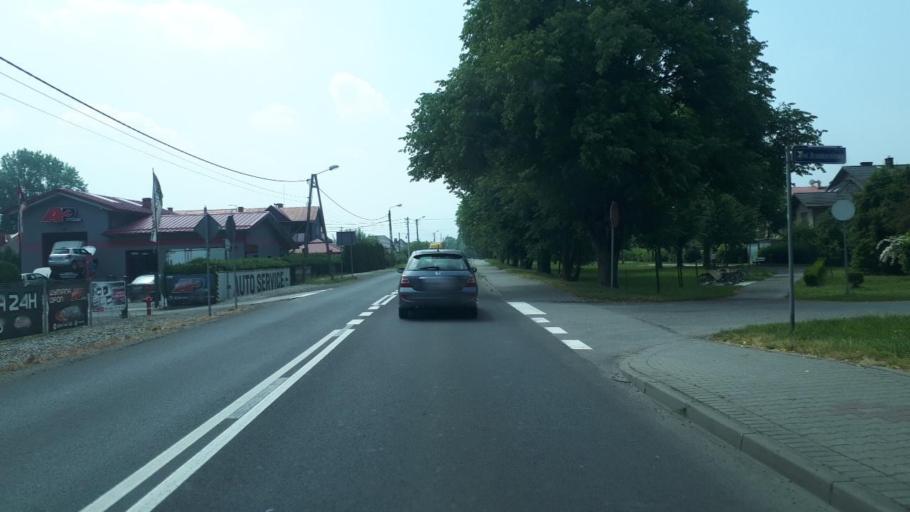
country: PL
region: Silesian Voivodeship
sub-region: Powiat cieszynski
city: Ustron
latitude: 49.7441
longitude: 18.8040
